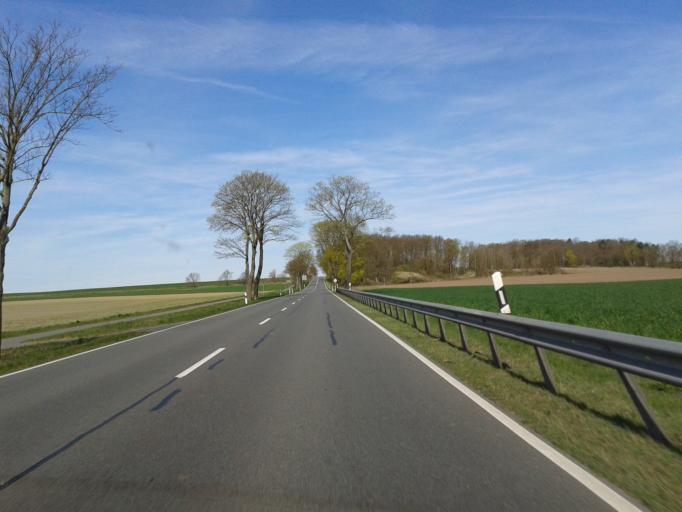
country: DE
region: Lower Saxony
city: Suhlendorf
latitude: 52.9409
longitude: 10.7414
